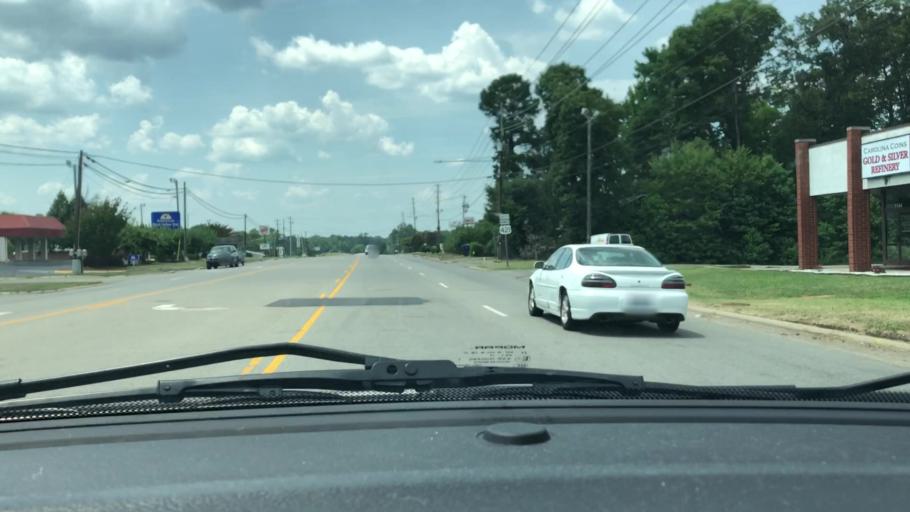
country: US
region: North Carolina
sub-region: Lee County
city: Sanford
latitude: 35.4961
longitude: -79.1965
